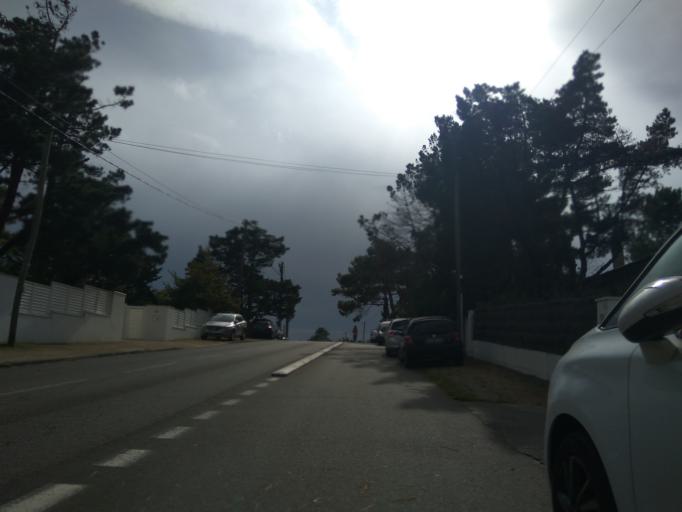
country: FR
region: Aquitaine
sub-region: Departement des Landes
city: Capbreton
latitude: 43.6448
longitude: -1.4408
